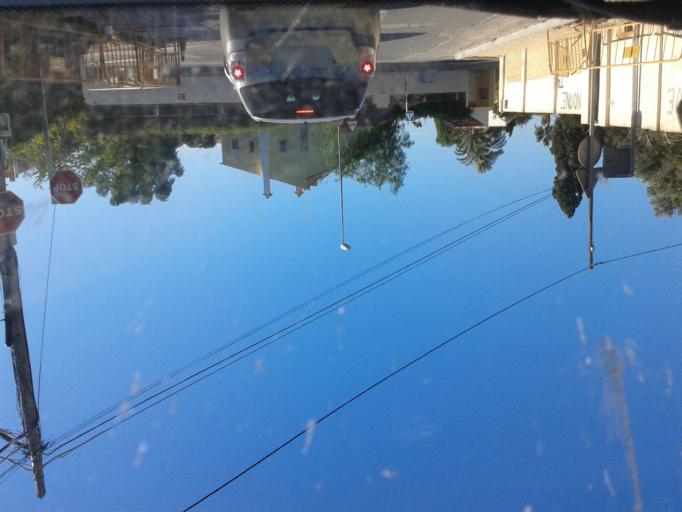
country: ES
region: Valencia
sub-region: Provincia de Alicante
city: el Campello
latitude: 38.4140
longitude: -0.4100
